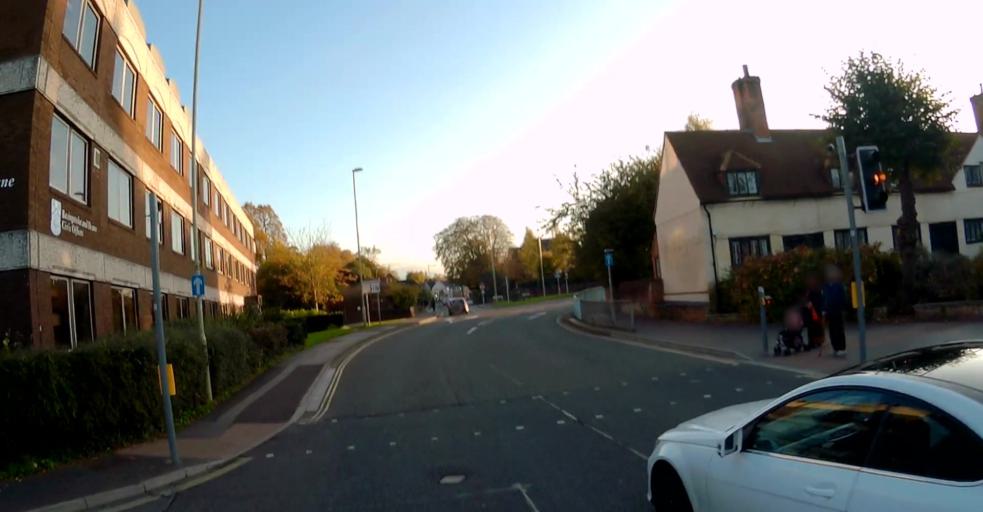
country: GB
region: England
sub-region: Hampshire
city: Basingstoke
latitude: 51.2624
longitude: -1.0841
